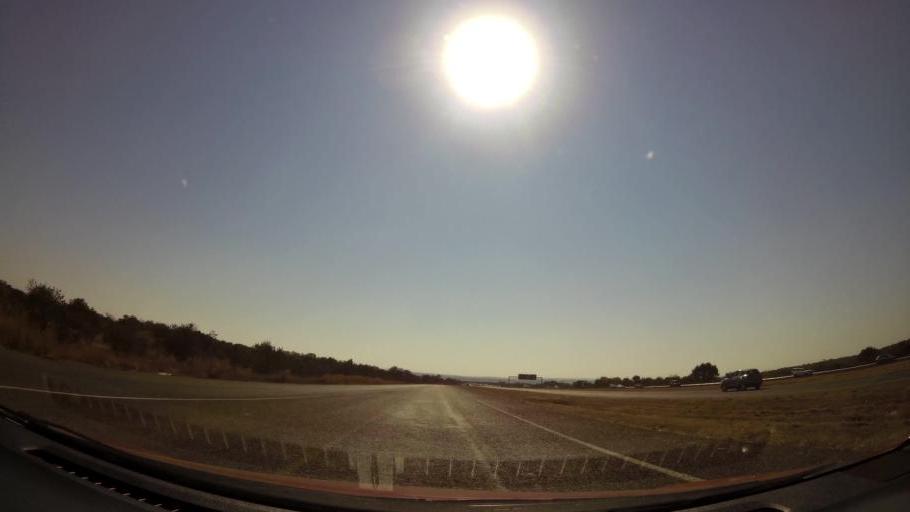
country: ZA
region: North-West
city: Ga-Rankuwa
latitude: -25.6243
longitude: 28.1111
